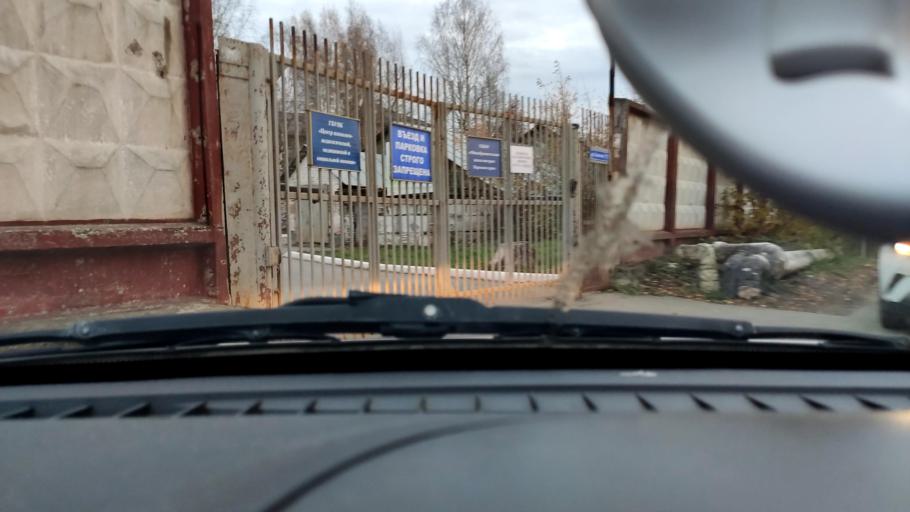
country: RU
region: Perm
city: Froly
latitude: 57.9750
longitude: 56.3132
